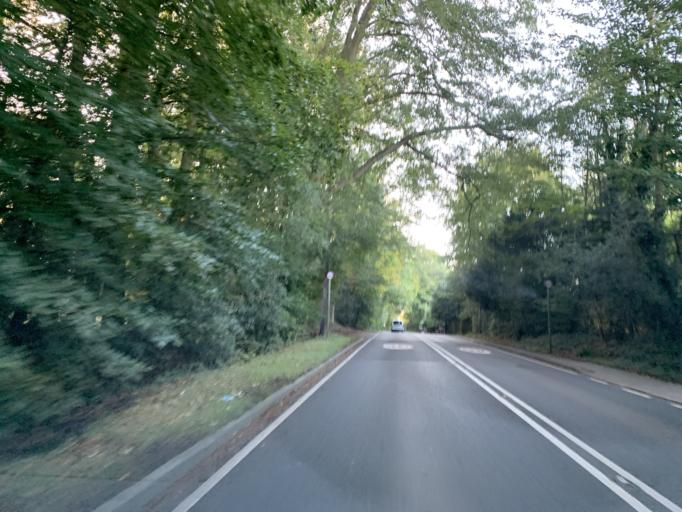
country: GB
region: England
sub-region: Hampshire
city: West Wellow
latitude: 50.9661
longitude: -1.5765
